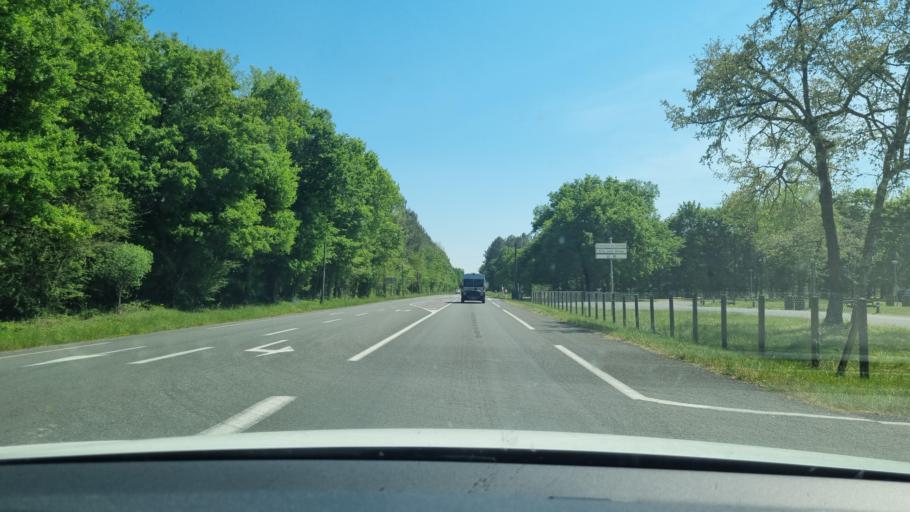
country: FR
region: Aquitaine
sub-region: Departement de la Gironde
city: Prechac
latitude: 44.2631
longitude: -0.2615
